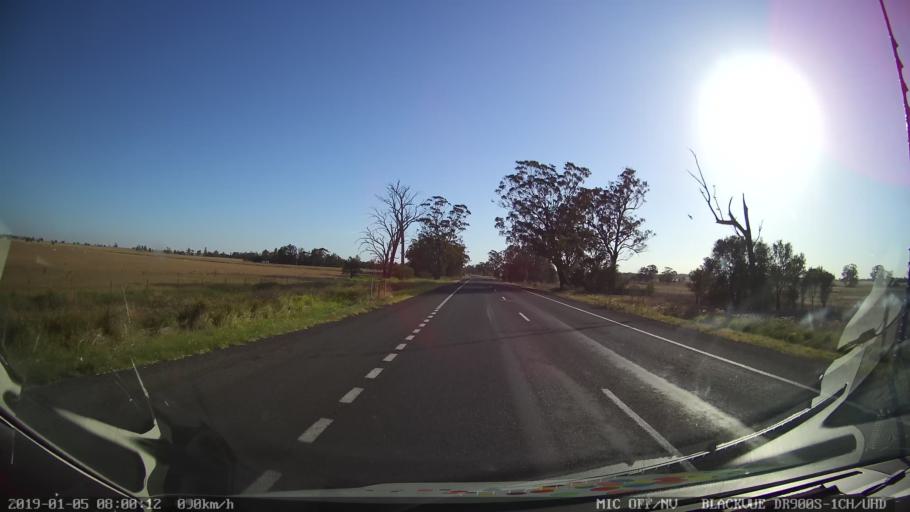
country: AU
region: New South Wales
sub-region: Gilgandra
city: Gilgandra
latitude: -31.6947
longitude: 148.6852
